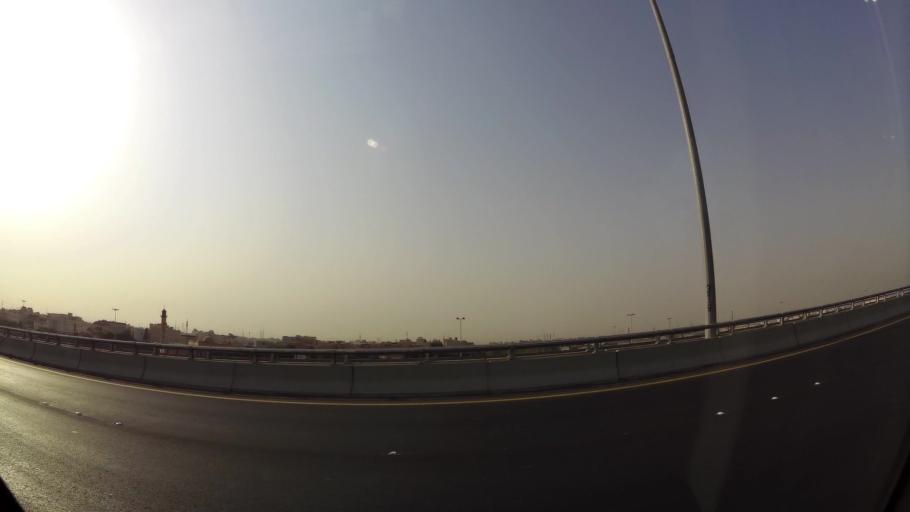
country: KW
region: Al Asimah
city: Ar Rabiyah
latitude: 29.3106
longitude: 47.8662
